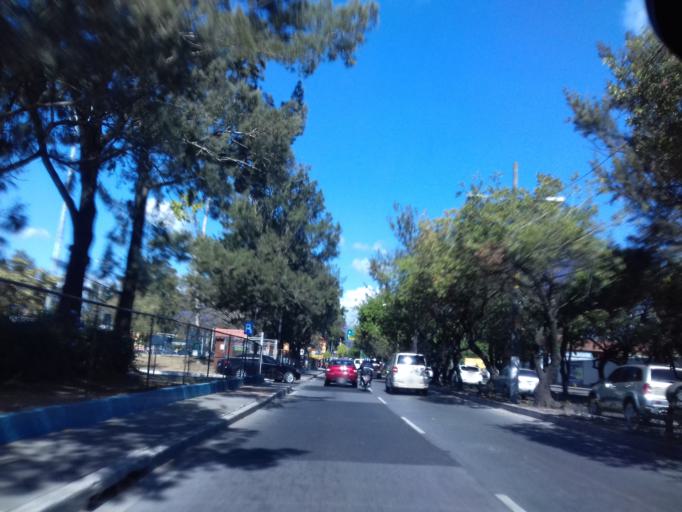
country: GT
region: Guatemala
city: Guatemala City
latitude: 14.6161
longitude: -90.5074
